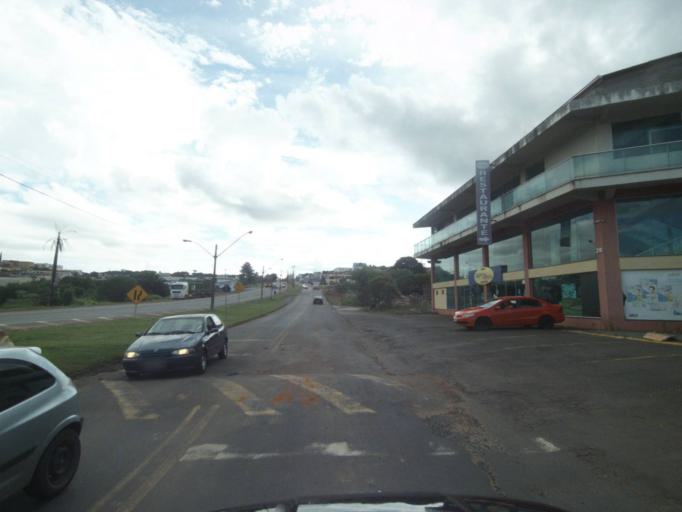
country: BR
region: Parana
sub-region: Telemaco Borba
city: Telemaco Borba
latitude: -24.3267
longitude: -50.6325
